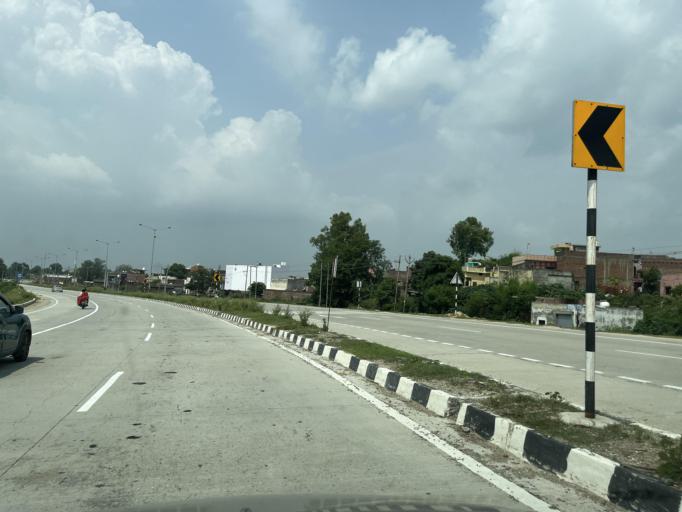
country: IN
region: Uttar Pradesh
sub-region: Bijnor
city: Sherkot
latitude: 29.3281
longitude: 78.5690
